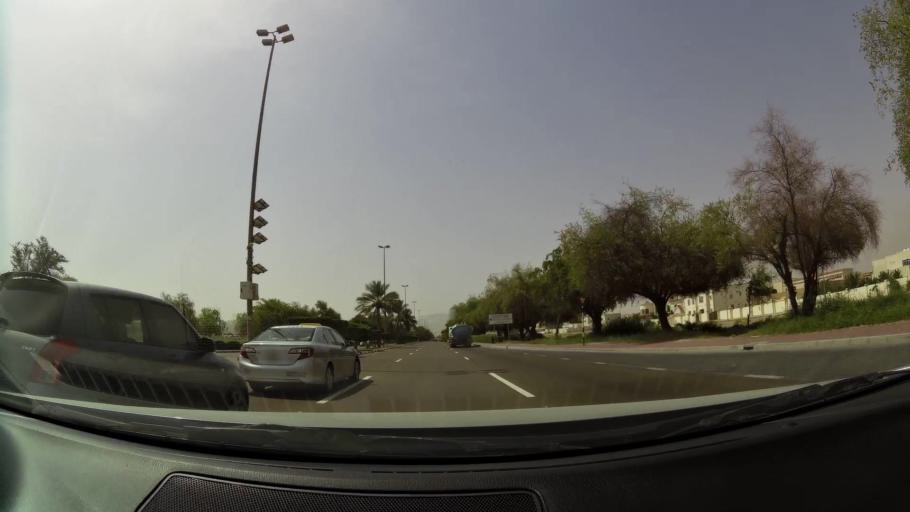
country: AE
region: Abu Dhabi
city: Al Ain
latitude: 24.1781
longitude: 55.7049
